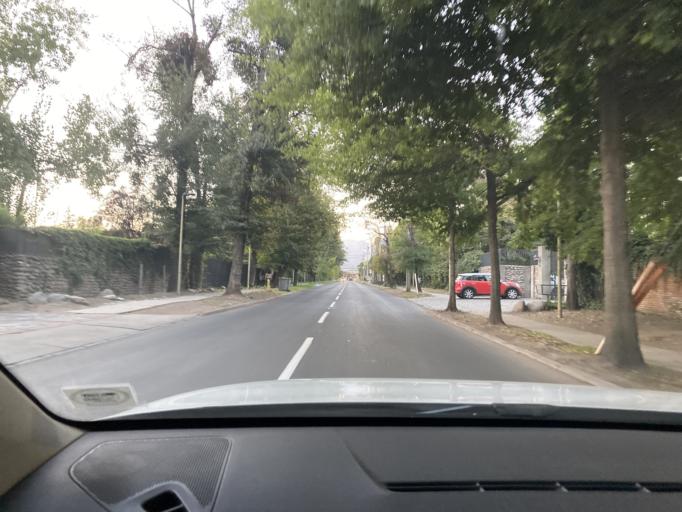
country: CL
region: Santiago Metropolitan
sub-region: Provincia de Santiago
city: Villa Presidente Frei, Nunoa, Santiago, Chile
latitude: -33.3738
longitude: -70.5059
